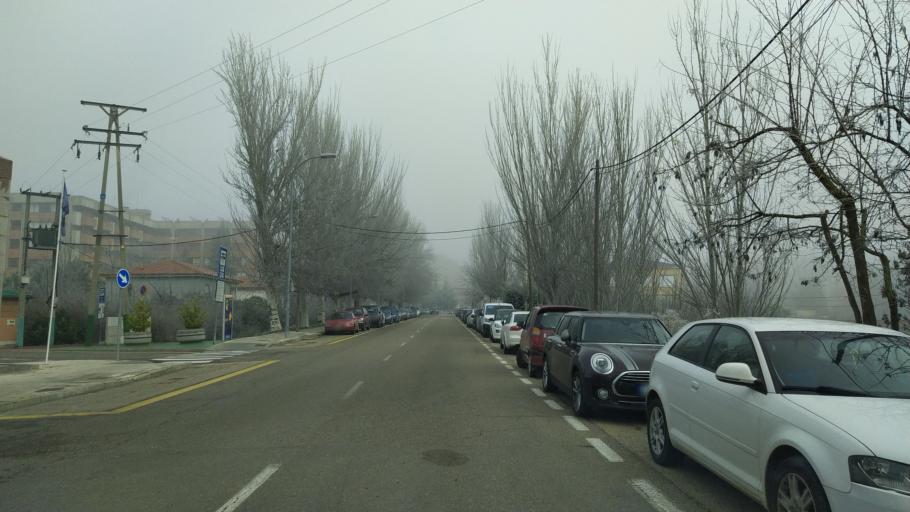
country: ES
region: Castille and Leon
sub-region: Provincia de Palencia
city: Palencia
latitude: 42.0030
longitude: -4.5347
